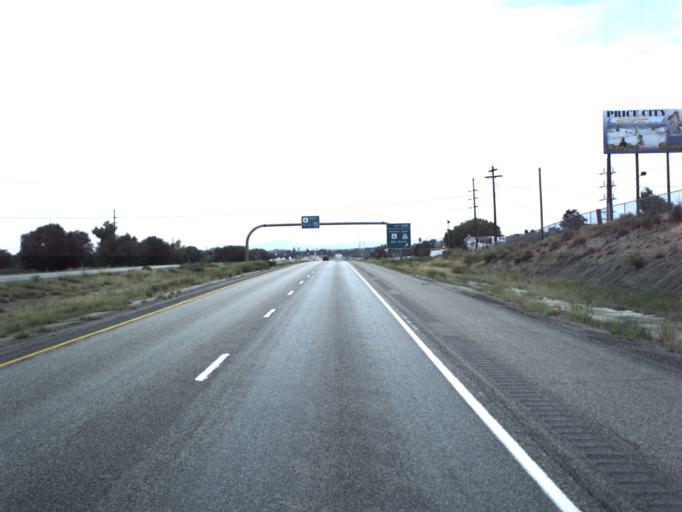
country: US
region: Utah
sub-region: Carbon County
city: Carbonville
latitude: 39.6104
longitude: -110.8353
